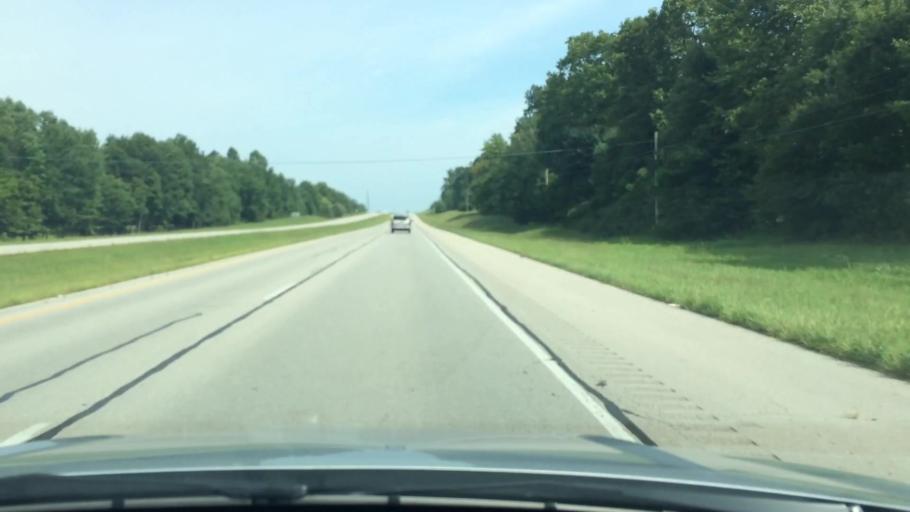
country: US
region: Kentucky
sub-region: Anderson County
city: Lawrenceburg
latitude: 38.0784
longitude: -84.9175
